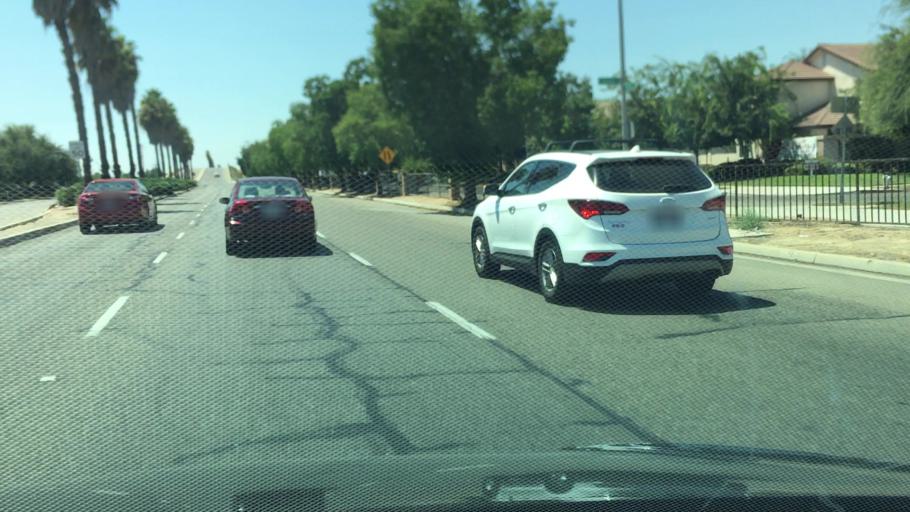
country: US
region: California
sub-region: Fresno County
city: West Park
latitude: 36.8371
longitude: -119.8800
